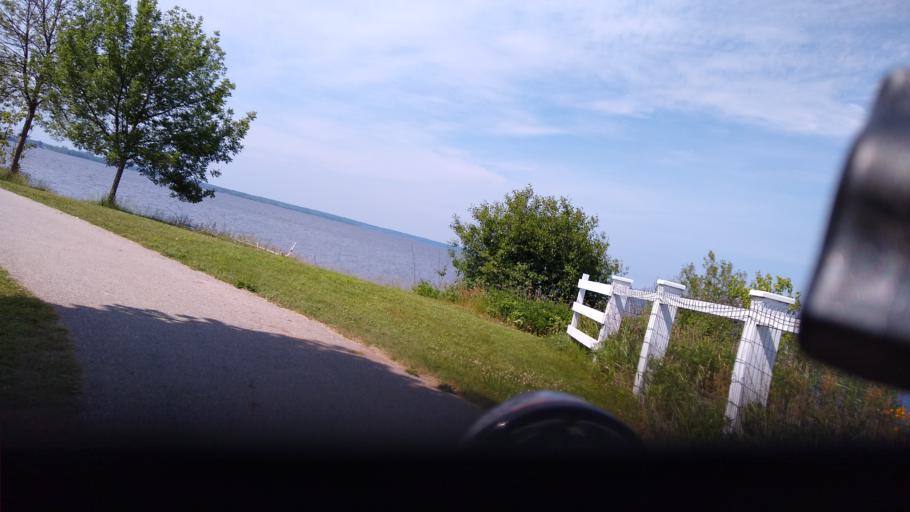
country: US
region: Michigan
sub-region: Delta County
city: Escanaba
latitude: 45.7450
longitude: -87.0447
